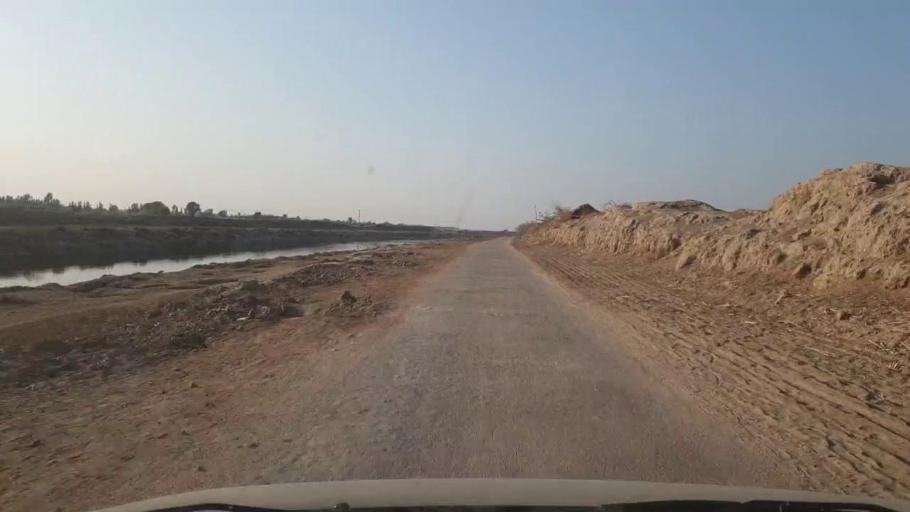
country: PK
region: Sindh
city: Samaro
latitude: 25.2868
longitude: 69.3358
